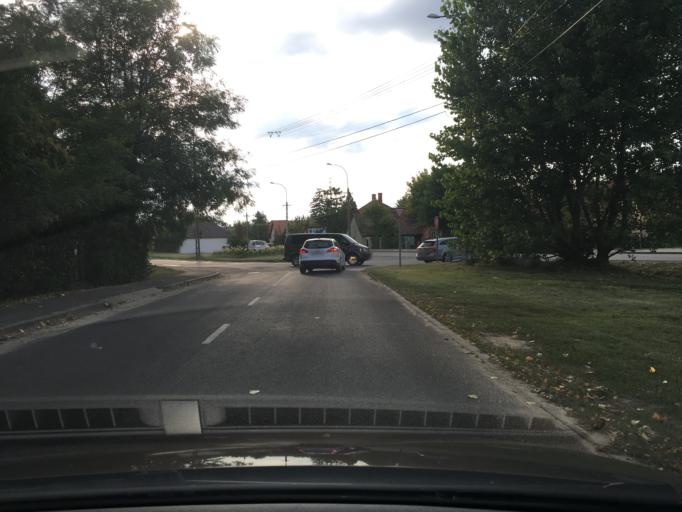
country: HU
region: Pest
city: Veresegyhaz
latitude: 47.6586
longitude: 19.2919
